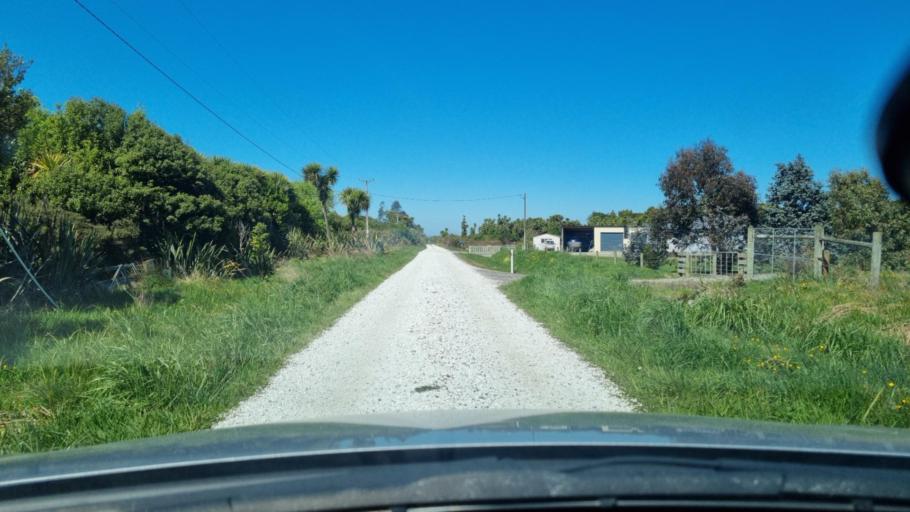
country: NZ
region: Southland
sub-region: Invercargill City
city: Invercargill
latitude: -46.4514
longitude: 168.3167
